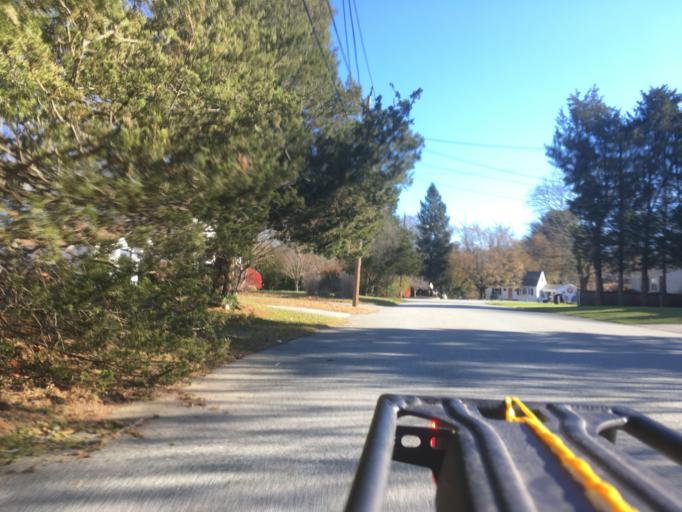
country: US
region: Rhode Island
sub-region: Kent County
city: East Greenwich
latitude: 41.6620
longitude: -71.4665
